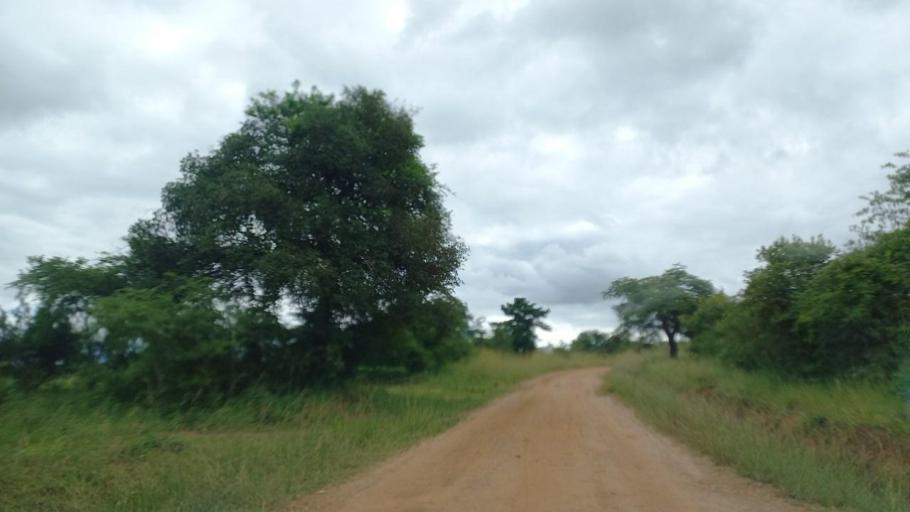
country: ZM
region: Lusaka
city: Chongwe
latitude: -15.4571
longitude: 28.8814
